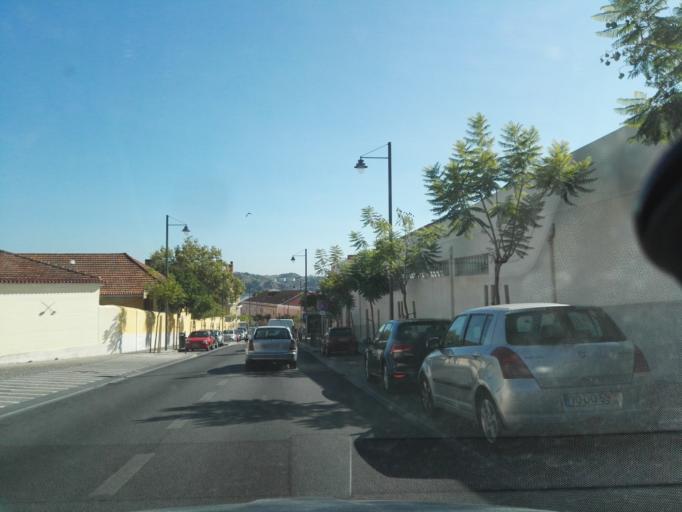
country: PT
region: Lisbon
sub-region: Oeiras
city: Alges
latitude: 38.7017
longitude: -9.1998
